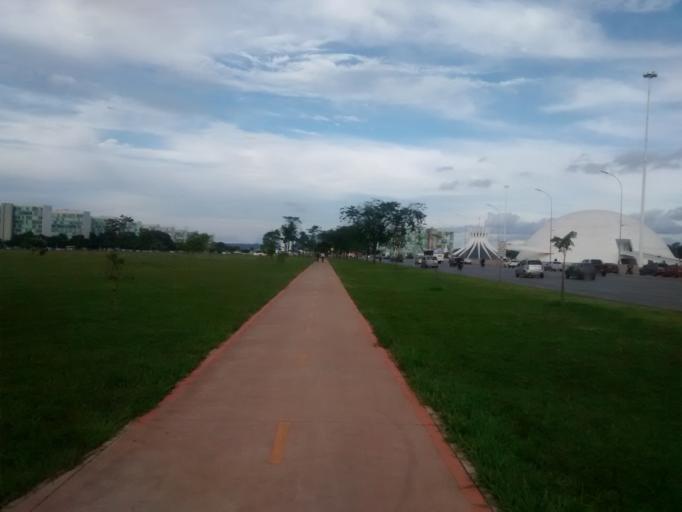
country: BR
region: Federal District
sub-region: Brasilia
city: Brasilia
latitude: -15.7954
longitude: -47.8805
